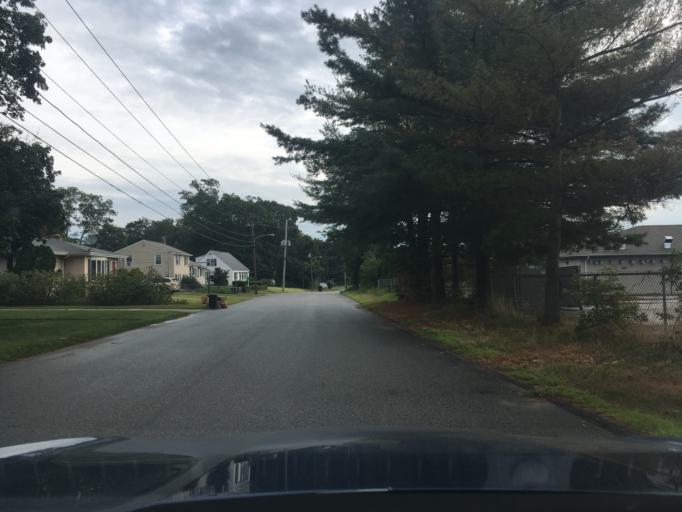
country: US
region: Rhode Island
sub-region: Kent County
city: East Greenwich
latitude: 41.6411
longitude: -71.4692
